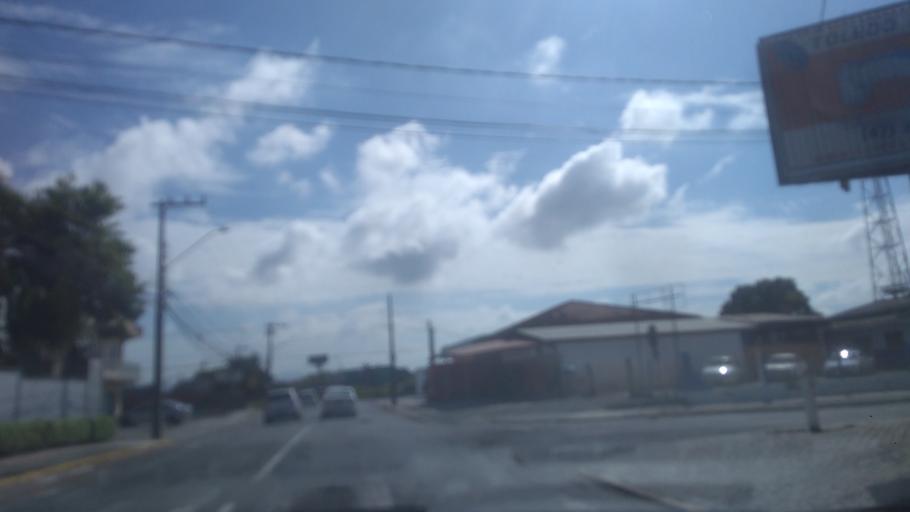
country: BR
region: Santa Catarina
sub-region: Joinville
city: Joinville
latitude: -26.3090
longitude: -48.8282
